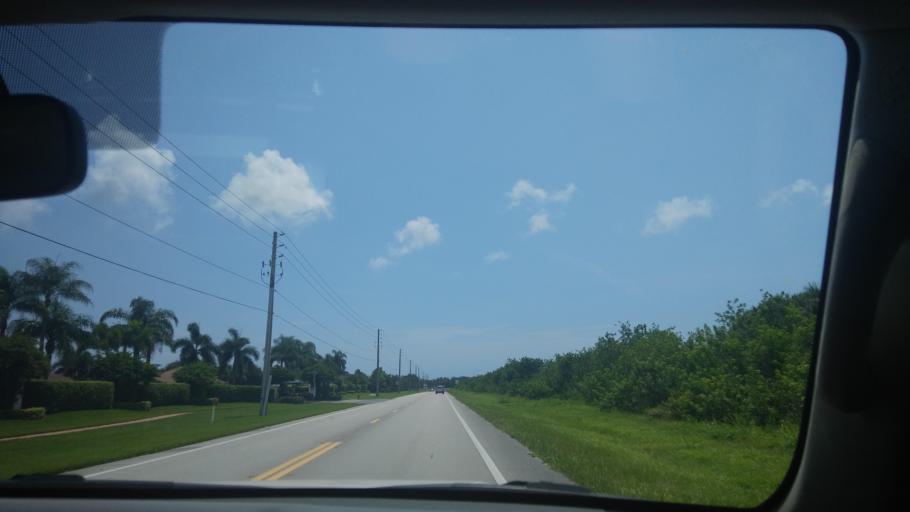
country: US
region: Florida
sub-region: Indian River County
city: Gifford
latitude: 27.6677
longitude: -80.4009
